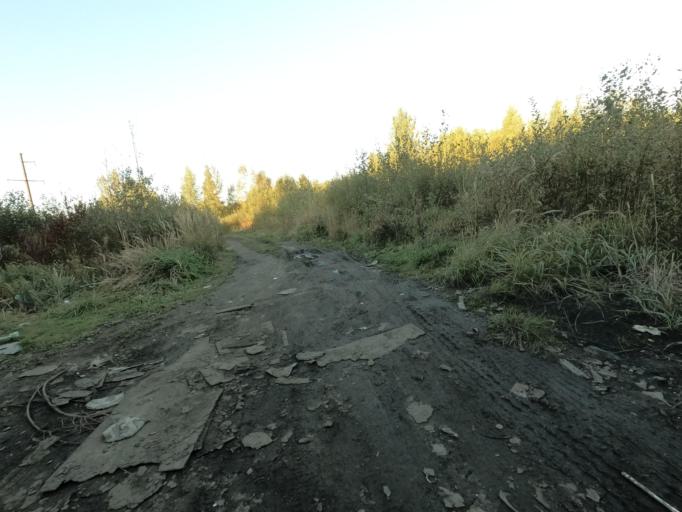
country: RU
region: Leningrad
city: Nikol'skoye
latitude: 59.7123
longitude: 30.7971
